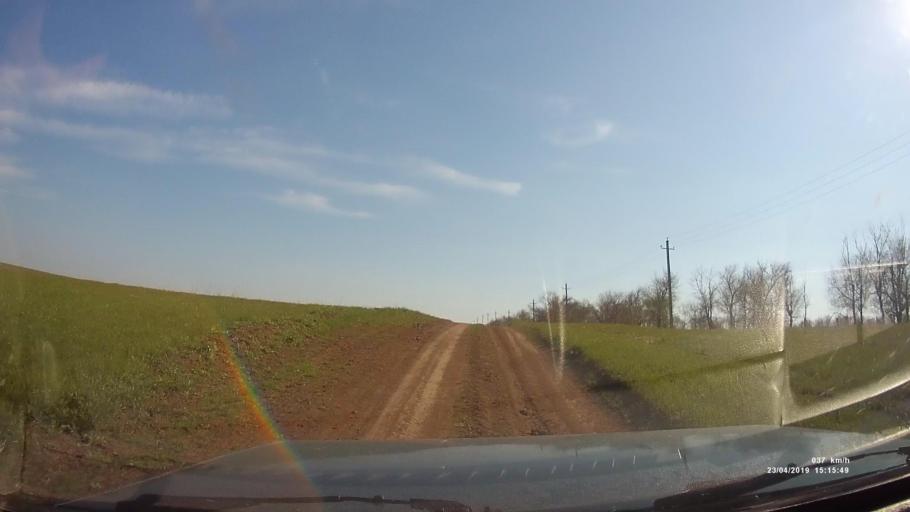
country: RU
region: Rostov
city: Remontnoye
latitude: 46.5372
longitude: 42.9697
